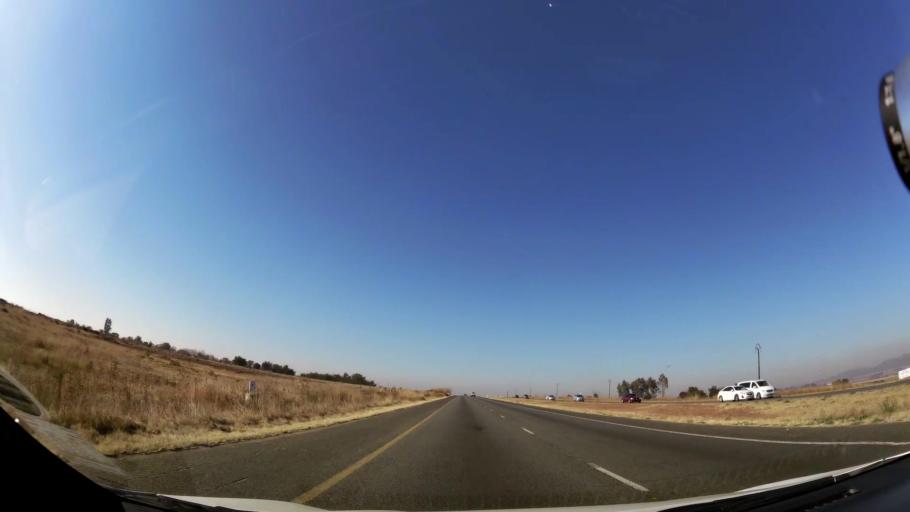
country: ZA
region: Gauteng
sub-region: City of Johannesburg Metropolitan Municipality
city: Johannesburg
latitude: -26.3214
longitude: 28.0664
